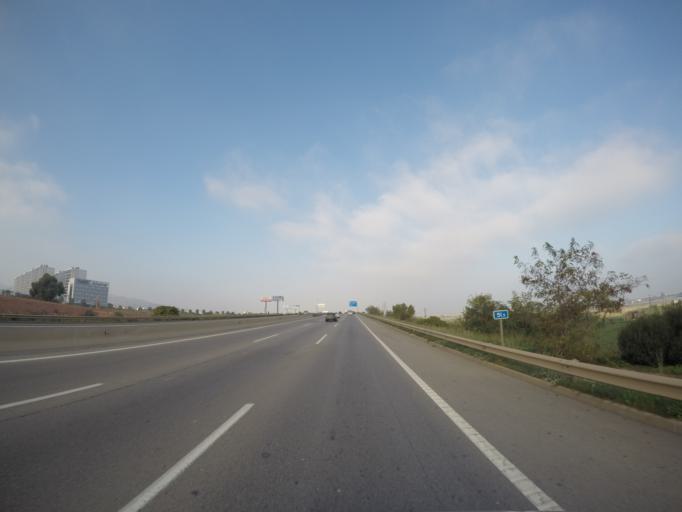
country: ES
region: Catalonia
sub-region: Provincia de Barcelona
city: Viladecans
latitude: 41.3079
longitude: 2.0287
